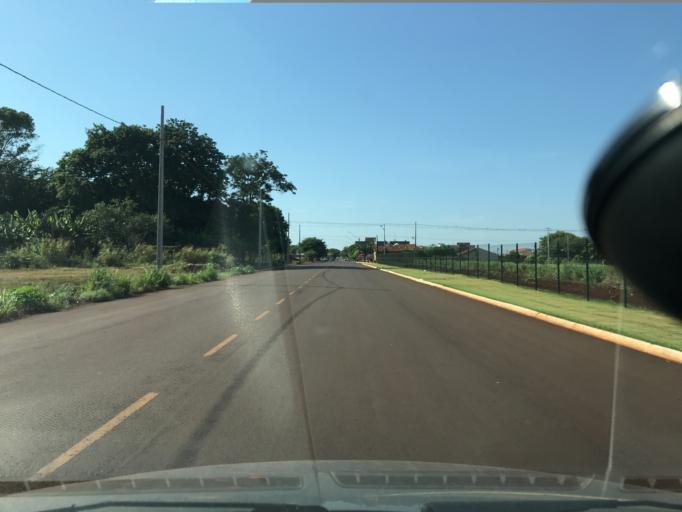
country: BR
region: Parana
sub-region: Palotina
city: Palotina
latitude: -24.2958
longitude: -53.8396
